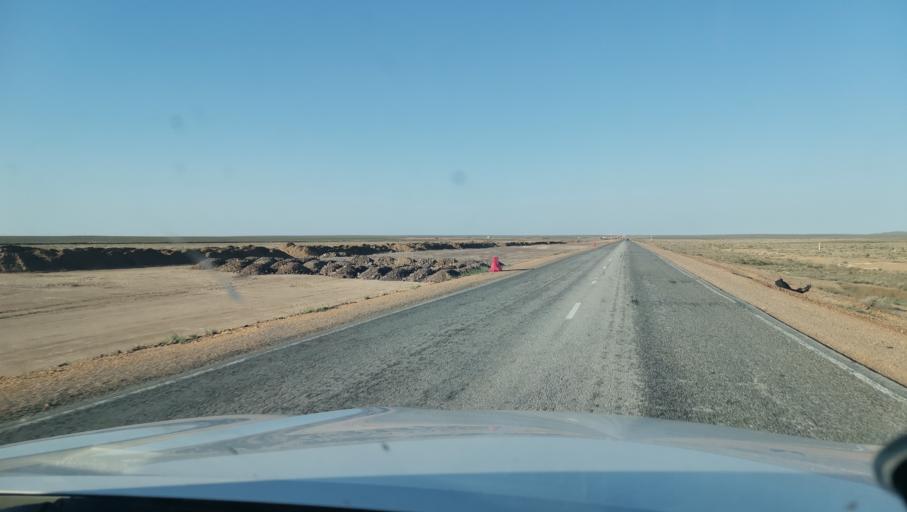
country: KZ
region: Qaraghandy
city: Saryshaghan
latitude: 46.4051
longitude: 73.8854
